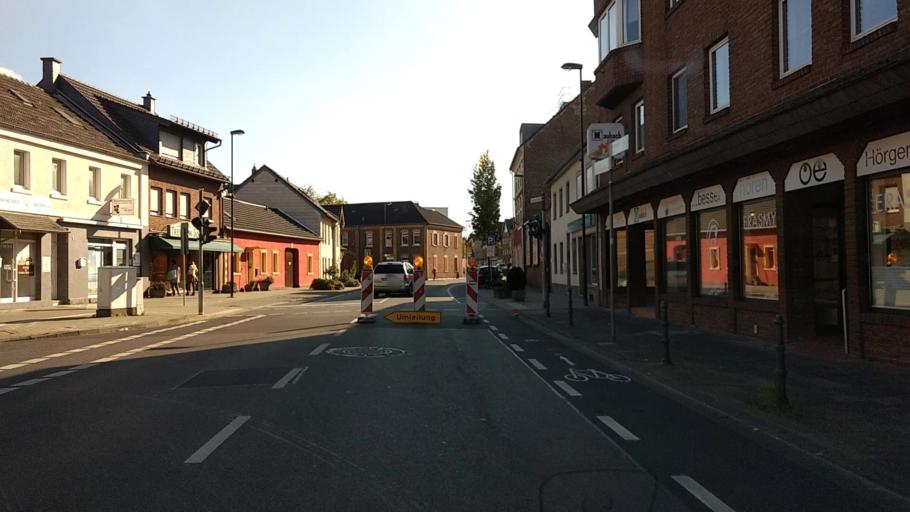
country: DE
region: North Rhine-Westphalia
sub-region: Regierungsbezirk Koln
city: Kerpen
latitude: 50.9085
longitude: 6.6725
